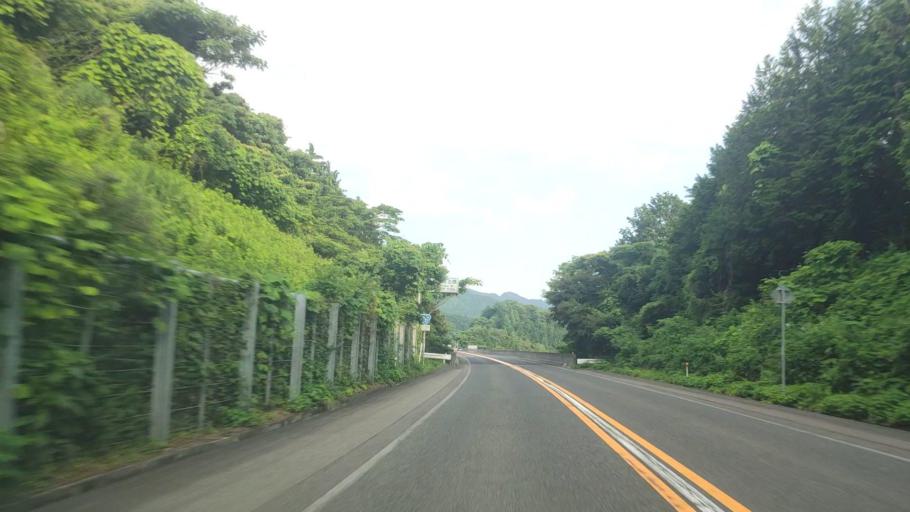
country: JP
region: Tottori
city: Kurayoshi
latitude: 35.3417
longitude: 133.7496
